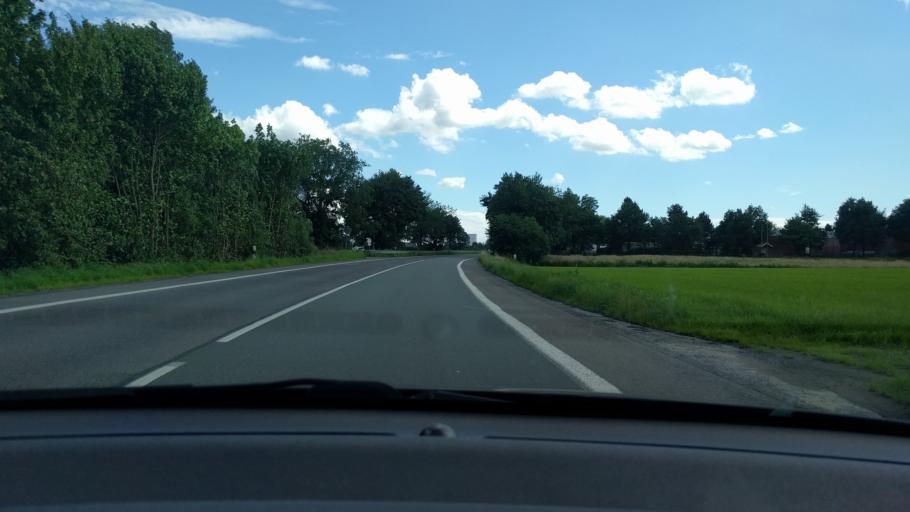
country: DE
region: North Rhine-Westphalia
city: Olfen
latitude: 51.6835
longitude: 7.3284
